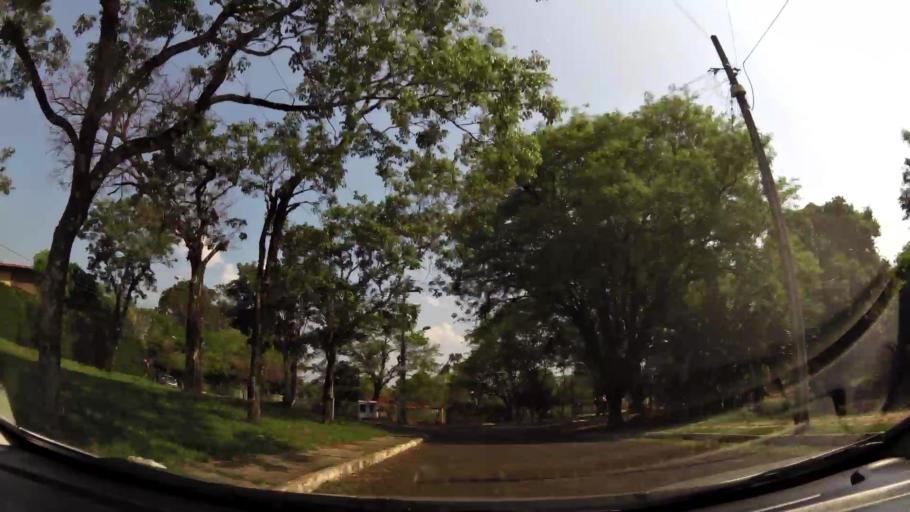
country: PY
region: Alto Parana
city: Presidente Franco
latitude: -25.5182
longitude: -54.6317
